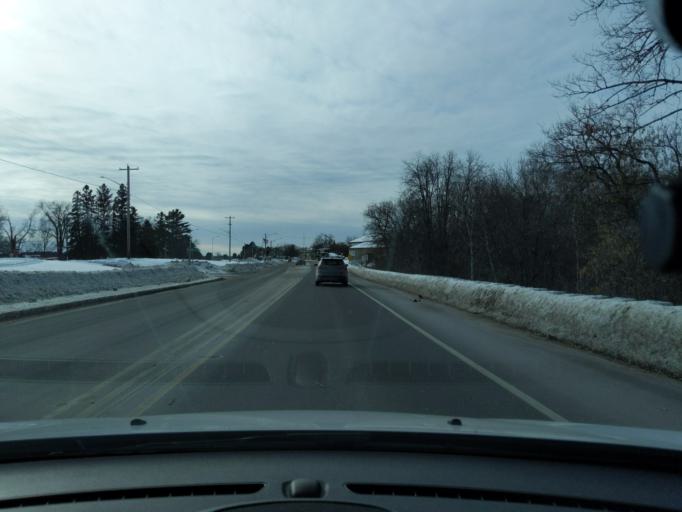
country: US
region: Wisconsin
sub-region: Washburn County
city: Shell Lake
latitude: 45.7454
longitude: -91.9212
